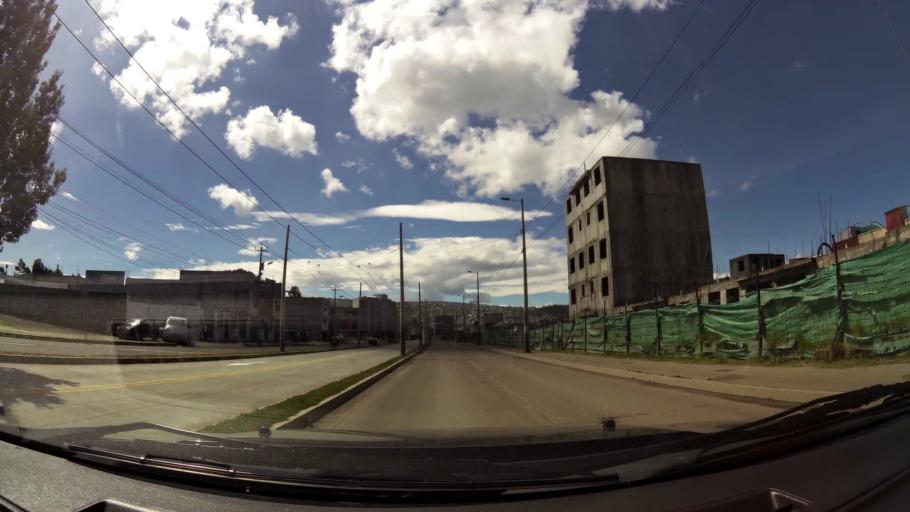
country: EC
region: Pichincha
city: Quito
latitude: -0.2973
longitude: -78.5521
